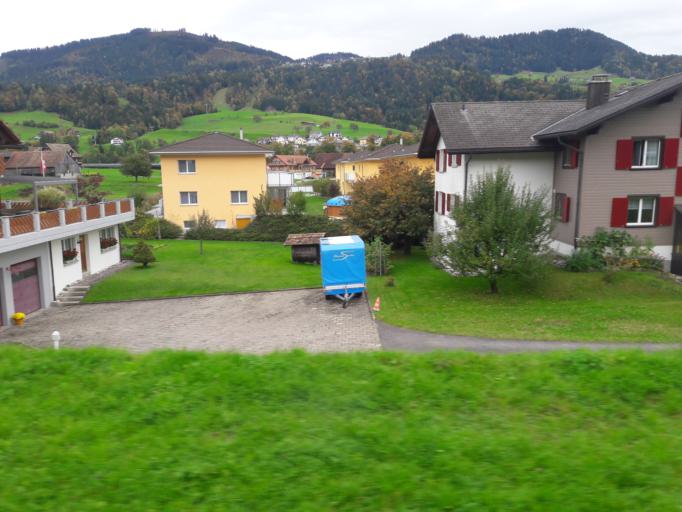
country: CH
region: Schwyz
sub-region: Bezirk Schwyz
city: Sattel
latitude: 47.0789
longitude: 8.6254
